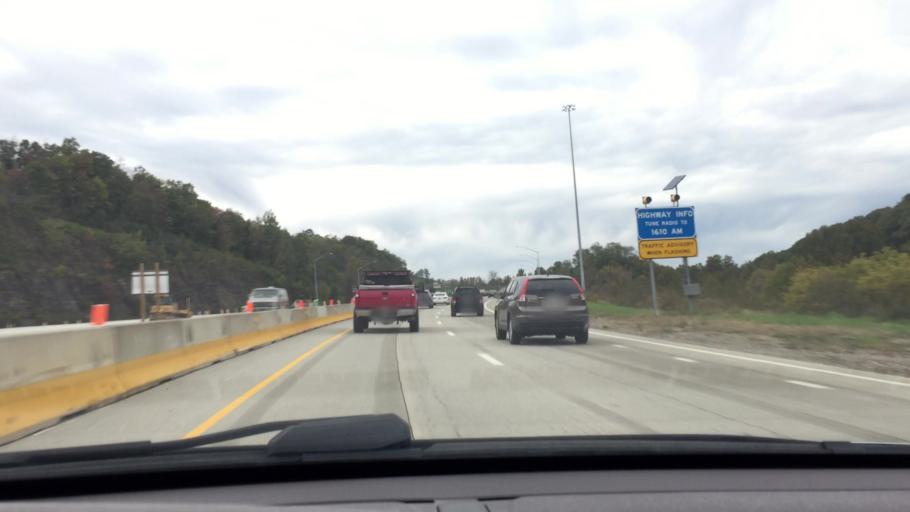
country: US
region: Pennsylvania
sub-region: Allegheny County
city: Enlow
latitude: 40.4692
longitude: -80.2051
